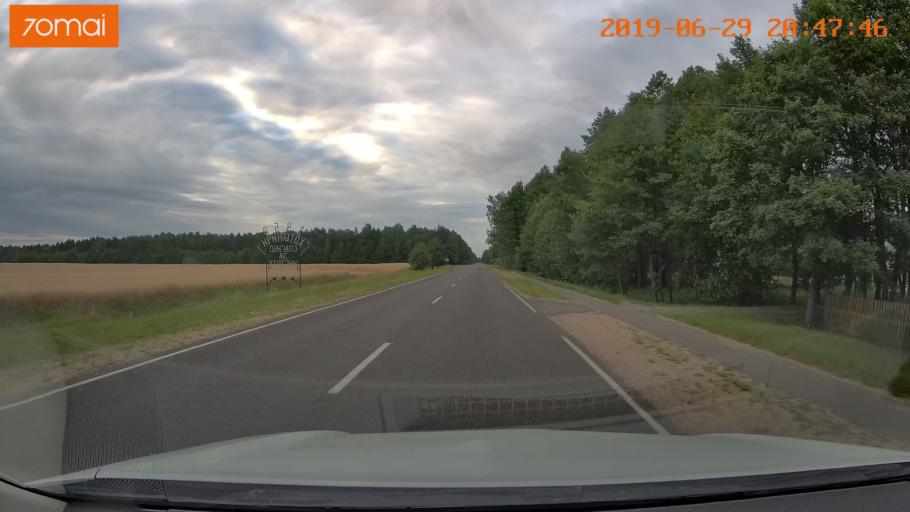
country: BY
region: Brest
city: Hantsavichy
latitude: 52.6420
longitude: 26.3162
